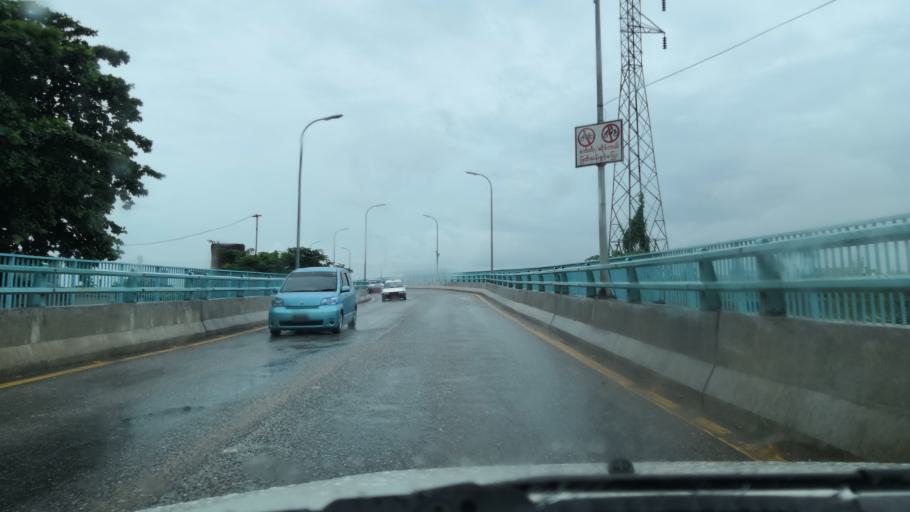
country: MM
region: Yangon
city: Yangon
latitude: 16.8063
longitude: 96.1875
